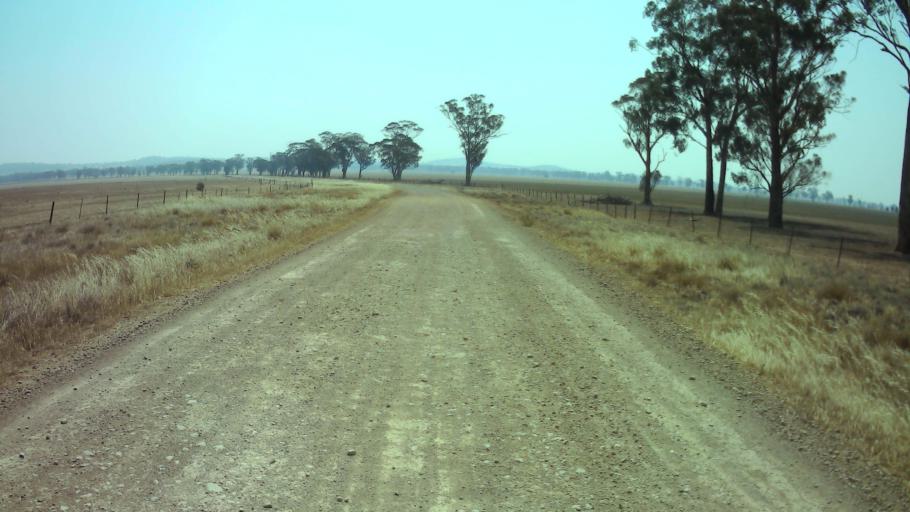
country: AU
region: New South Wales
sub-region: Weddin
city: Grenfell
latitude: -33.6371
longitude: 148.2363
